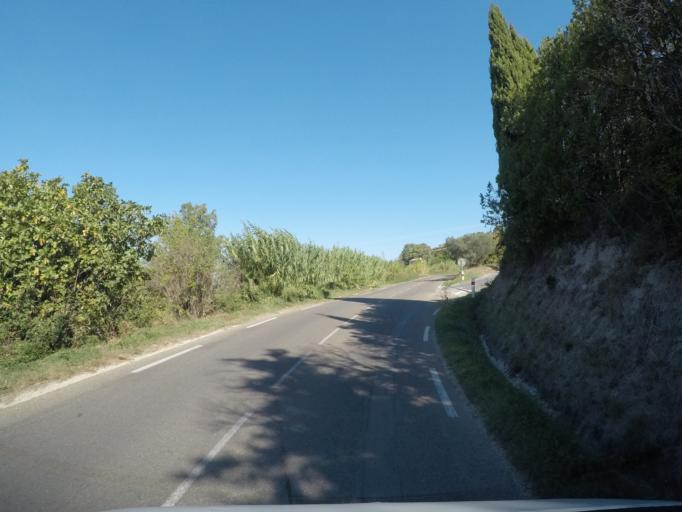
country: FR
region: Languedoc-Roussillon
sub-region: Departement du Gard
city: Uzes
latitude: 44.0055
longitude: 4.4043
